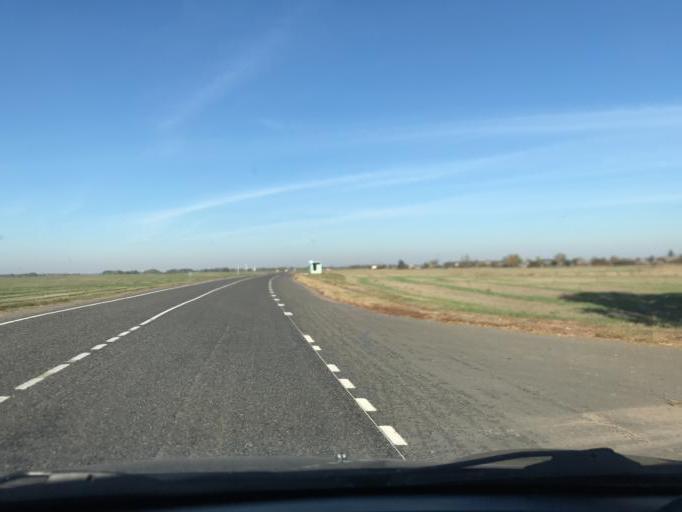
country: BY
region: Gomel
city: Brahin
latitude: 51.6596
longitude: 30.4321
